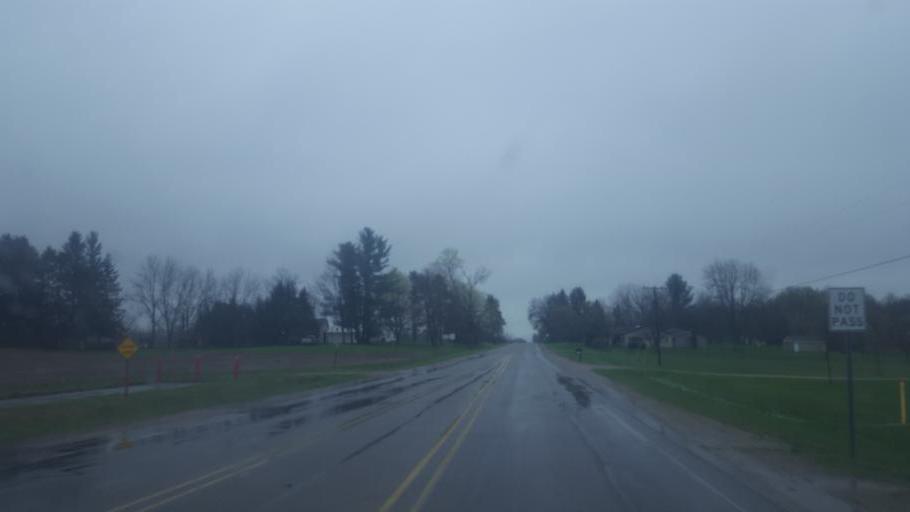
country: US
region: Michigan
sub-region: Isabella County
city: Mount Pleasant
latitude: 43.6400
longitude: -84.7682
